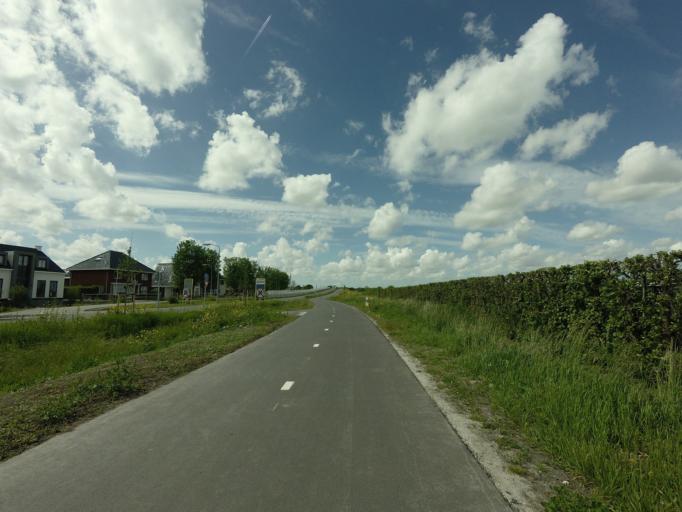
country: NL
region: North Holland
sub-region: Gemeente Hoorn
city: Hoorn
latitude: 52.6780
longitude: 5.0928
